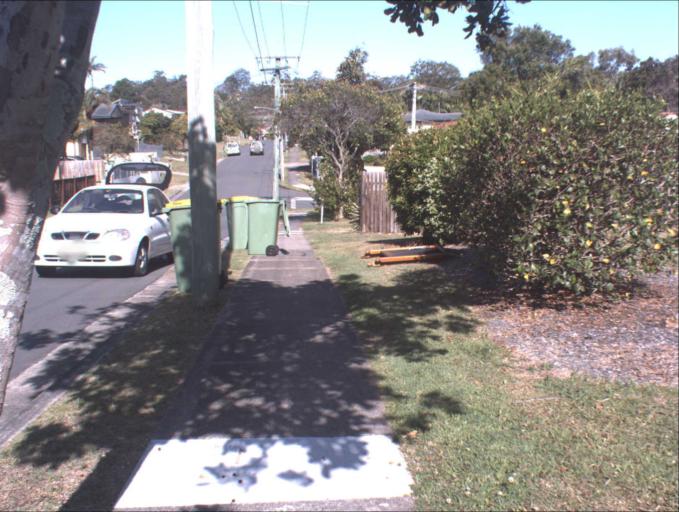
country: AU
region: Queensland
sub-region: Logan
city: Rochedale South
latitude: -27.6013
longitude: 153.1172
